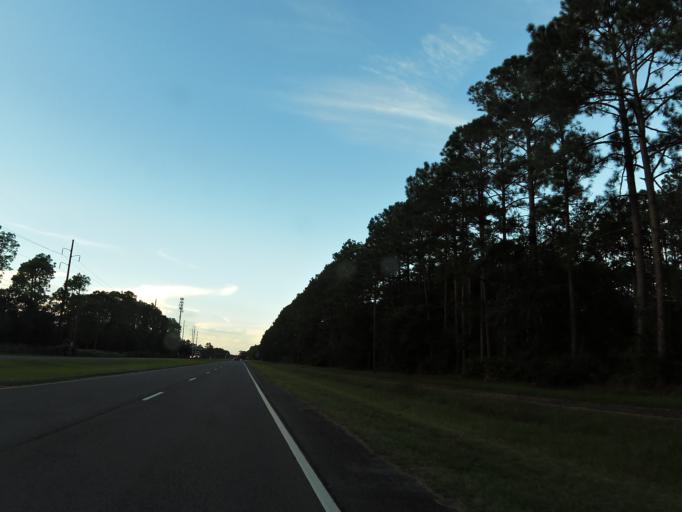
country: US
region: Georgia
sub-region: Camden County
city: St Marys
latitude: 30.7772
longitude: -81.5764
